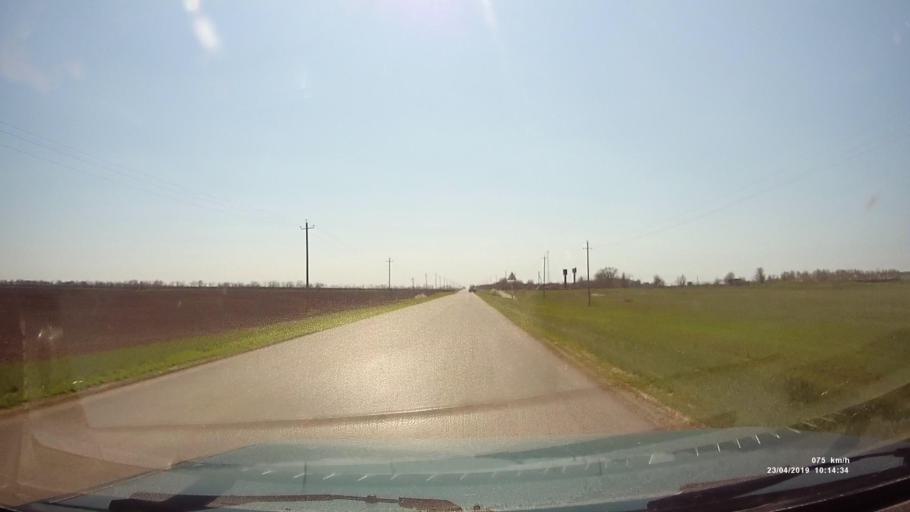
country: RU
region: Rostov
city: Sovetskoye
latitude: 46.6756
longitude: 42.3710
